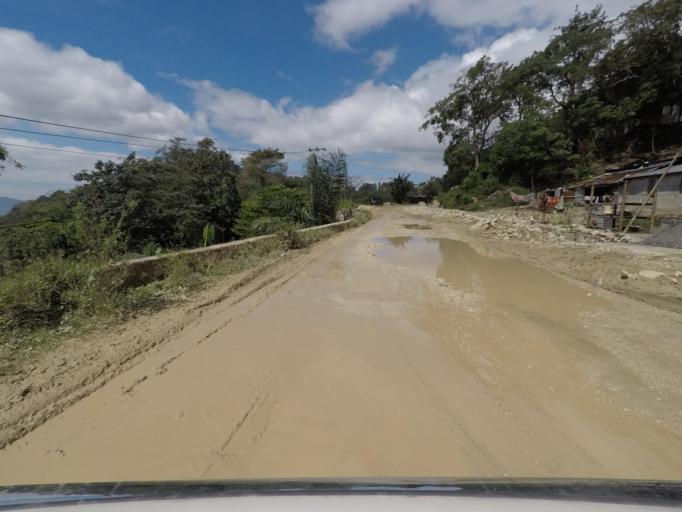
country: TL
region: Baucau
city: Venilale
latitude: -8.7194
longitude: 126.3674
